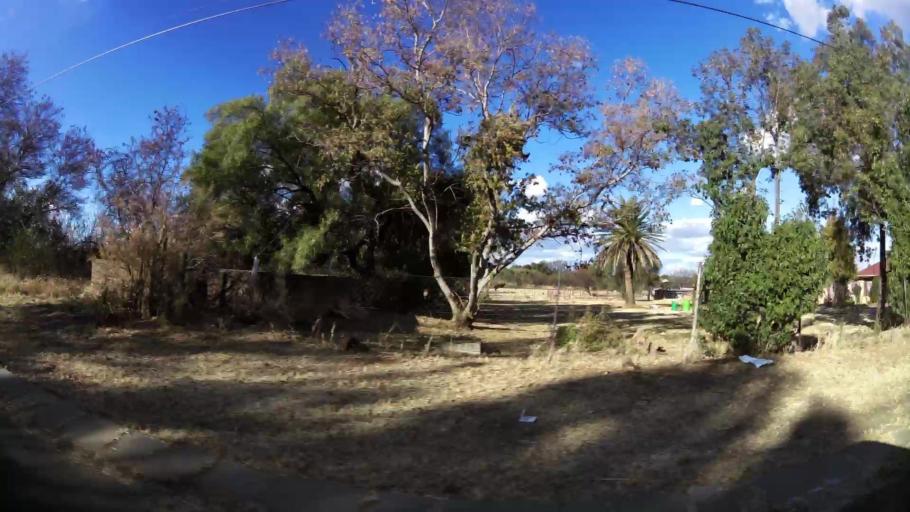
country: ZA
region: North-West
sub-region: Dr Kenneth Kaunda District Municipality
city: Klerksdorp
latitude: -26.8364
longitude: 26.6623
